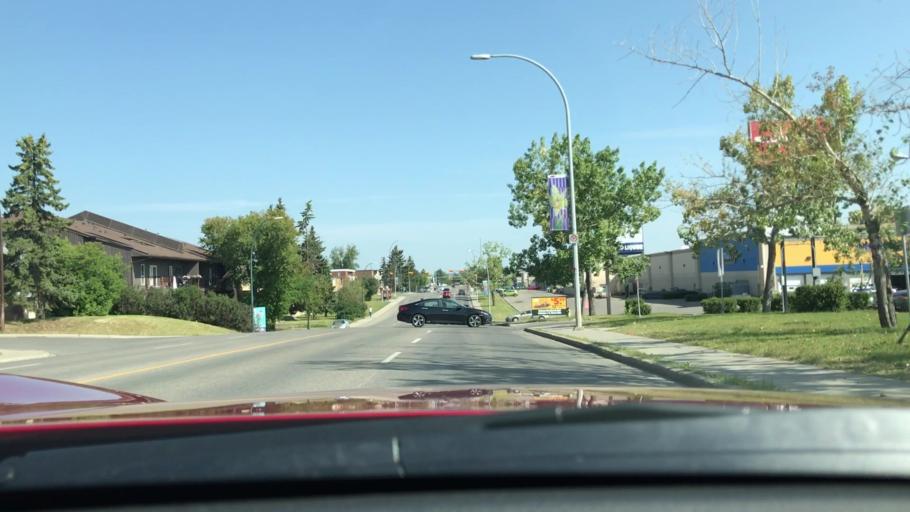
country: CA
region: Alberta
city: Calgary
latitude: 51.0392
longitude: -114.1412
